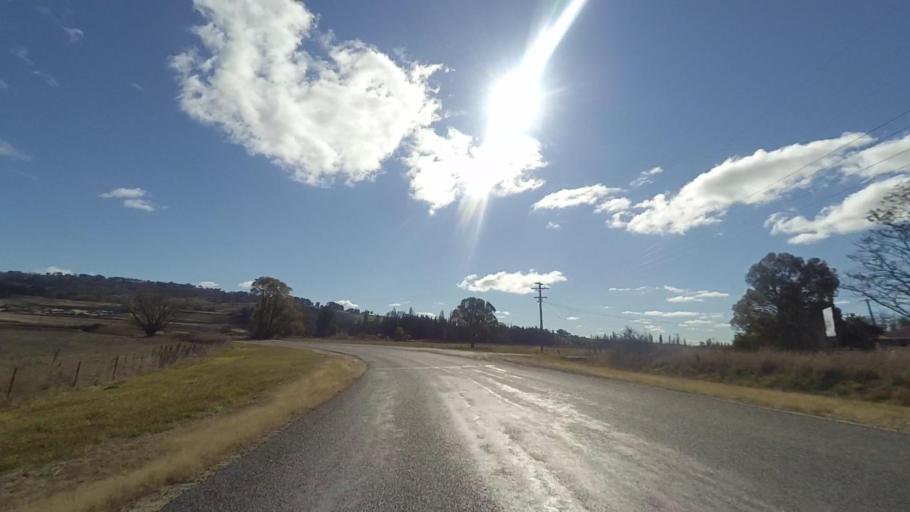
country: AU
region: New South Wales
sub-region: Bathurst Regional
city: Perthville
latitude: -33.4672
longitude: 149.5733
